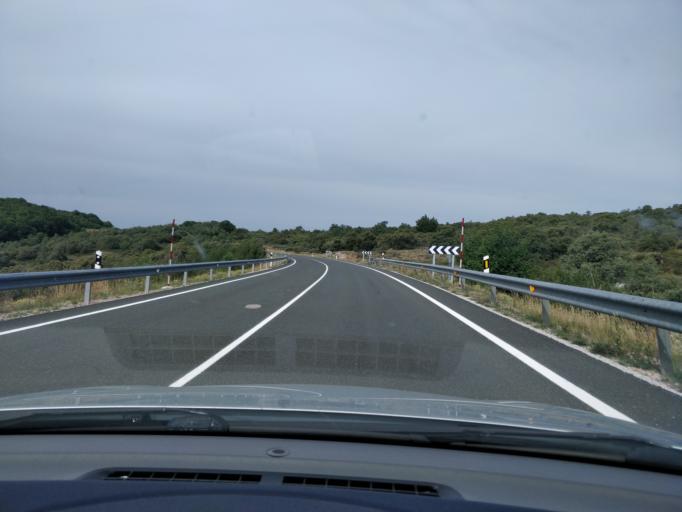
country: ES
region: Castille and Leon
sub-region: Provincia de Burgos
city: Espinosa de los Monteros
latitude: 42.9417
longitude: -3.6927
